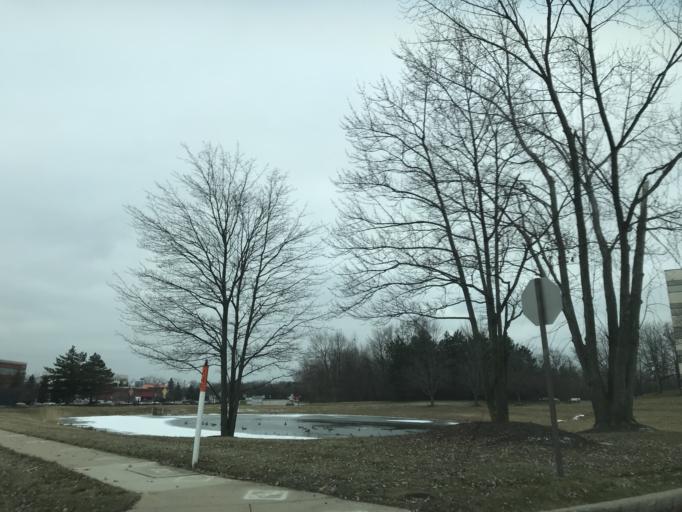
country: US
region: Michigan
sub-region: Oakland County
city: Troy
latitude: 42.5991
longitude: -83.1715
